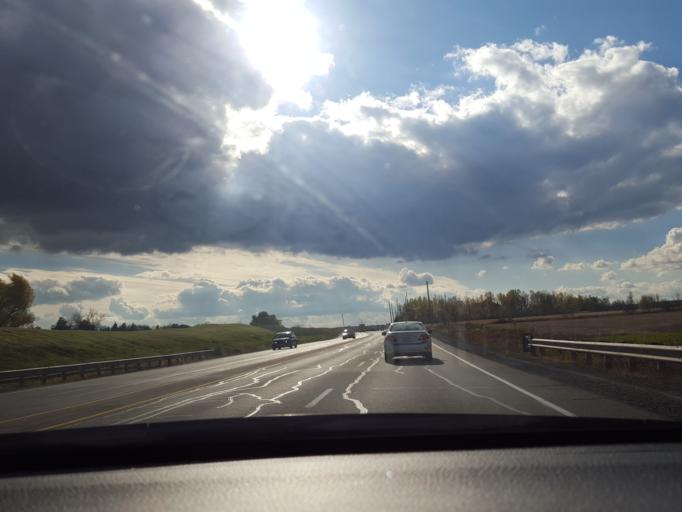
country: CA
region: Ontario
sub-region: Halton
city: Milton
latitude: 43.5421
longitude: -79.8228
